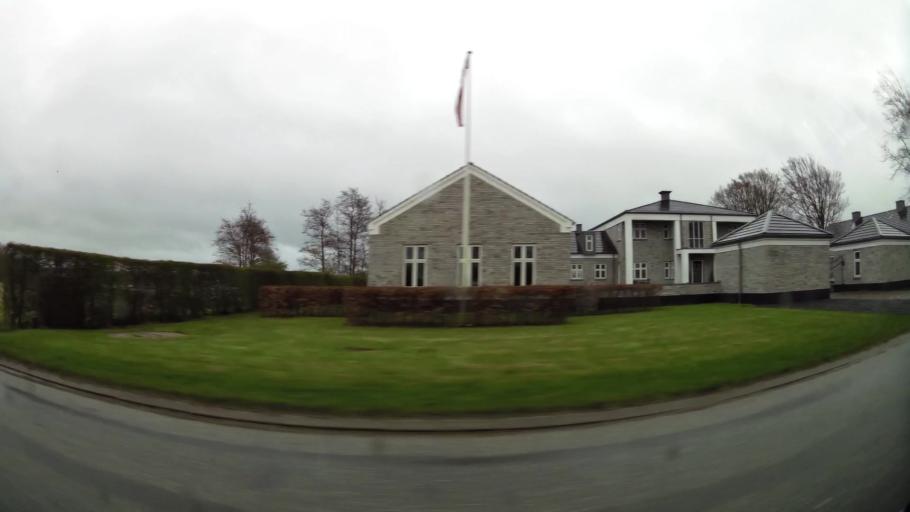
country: DK
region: Central Jutland
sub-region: Herning Kommune
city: Snejbjerg
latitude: 56.1587
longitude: 8.8972
